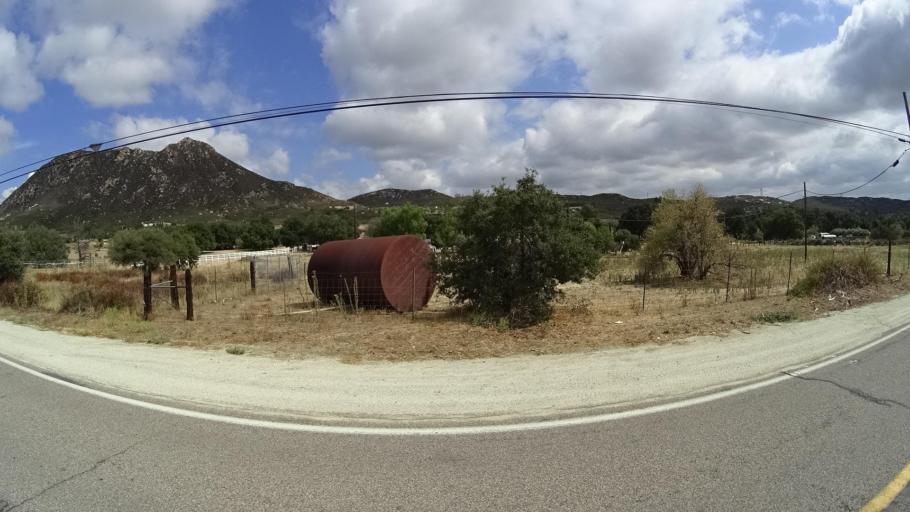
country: US
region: California
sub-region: San Diego County
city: Campo
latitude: 32.6752
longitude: -116.4887
